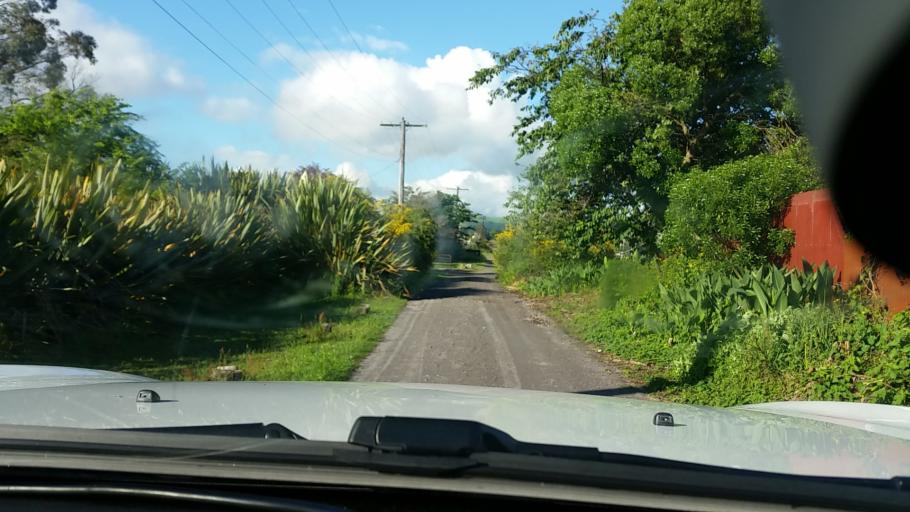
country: NZ
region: Bay of Plenty
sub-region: Rotorua District
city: Rotorua
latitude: -38.1452
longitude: 176.2704
